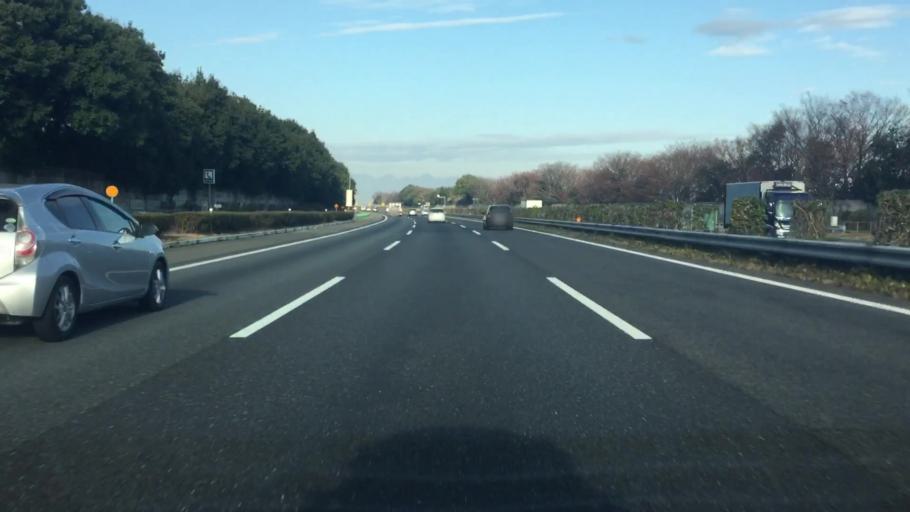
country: JP
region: Saitama
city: Honjo
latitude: 36.2453
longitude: 139.1418
